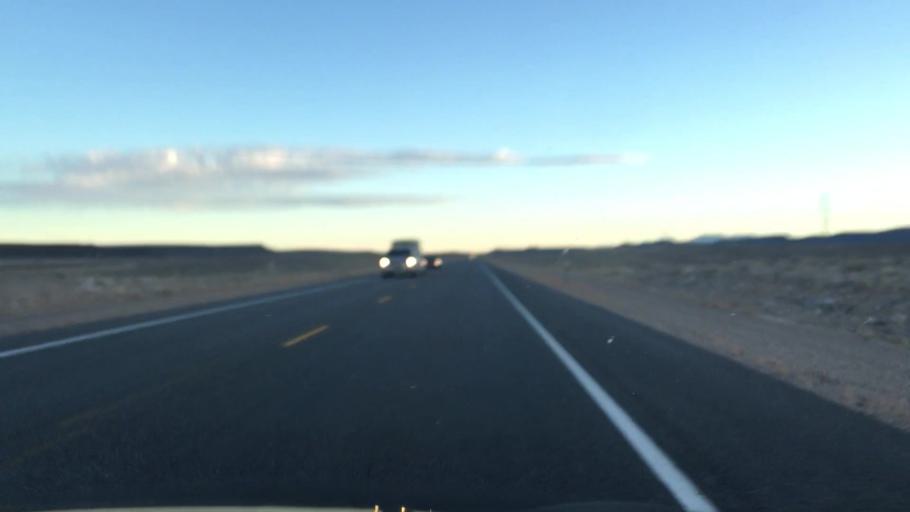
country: US
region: Nevada
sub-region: Esmeralda County
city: Goldfield
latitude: 37.4525
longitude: -117.1693
